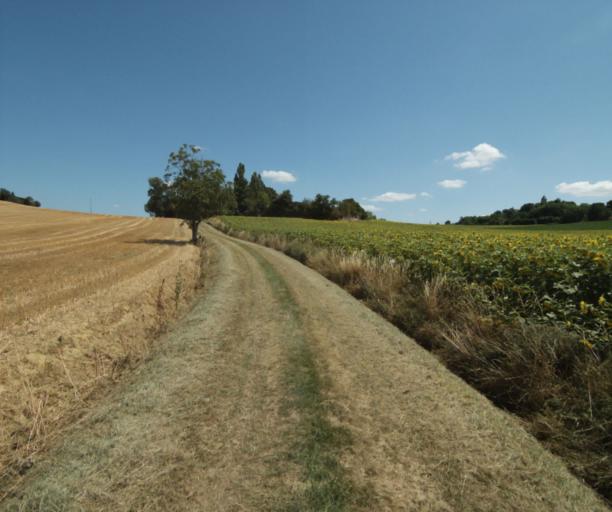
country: FR
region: Midi-Pyrenees
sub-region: Departement de la Haute-Garonne
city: Saint-Felix-Lauragais
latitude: 43.4557
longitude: 1.8890
